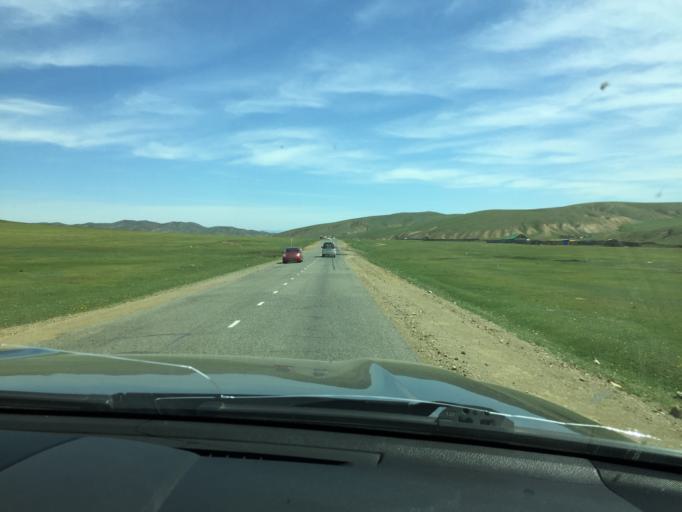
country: MN
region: Central Aimak
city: Bornuur
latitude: 48.6637
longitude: 106.1266
